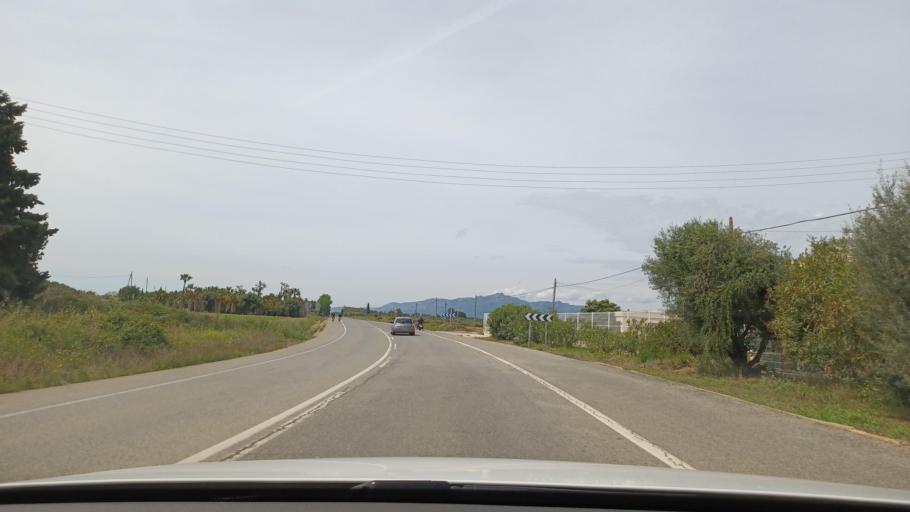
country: ES
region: Catalonia
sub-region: Provincia de Tarragona
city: Cambrils
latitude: 41.0579
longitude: 1.0108
